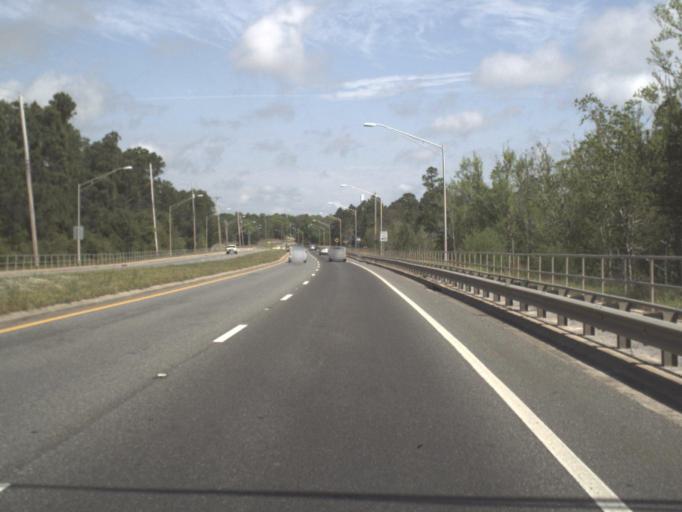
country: US
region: Florida
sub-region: Santa Rosa County
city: Navarre
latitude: 30.4380
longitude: -86.8656
